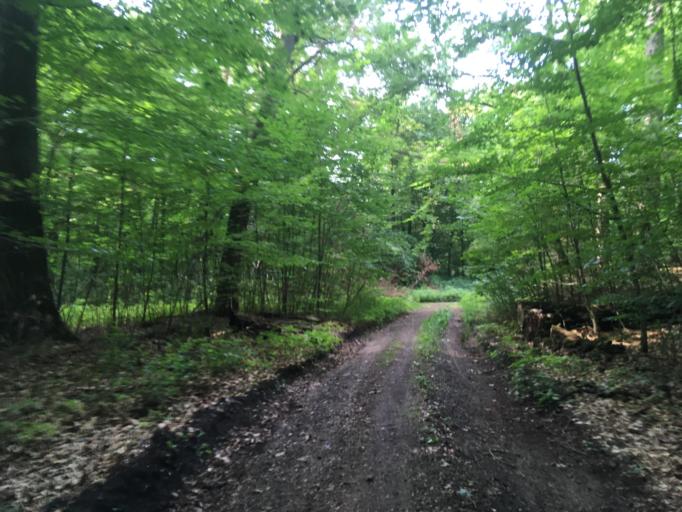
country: DE
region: Brandenburg
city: Eberswalde
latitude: 52.8131
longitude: 13.8181
